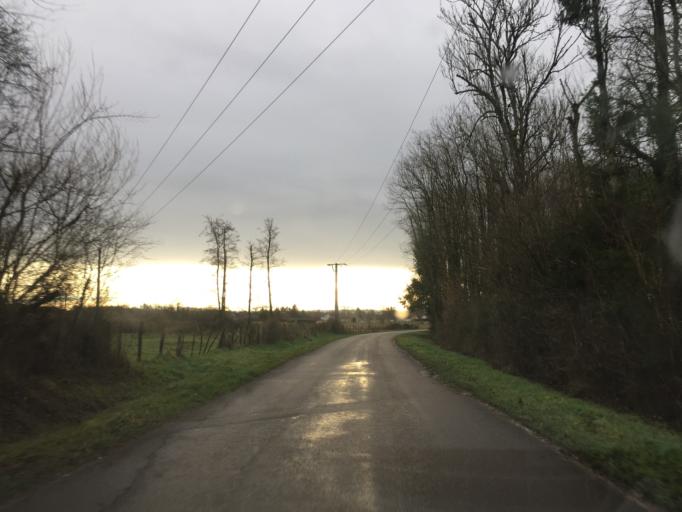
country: FR
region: Franche-Comte
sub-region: Departement du Jura
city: Choisey
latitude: 47.0446
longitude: 5.5070
